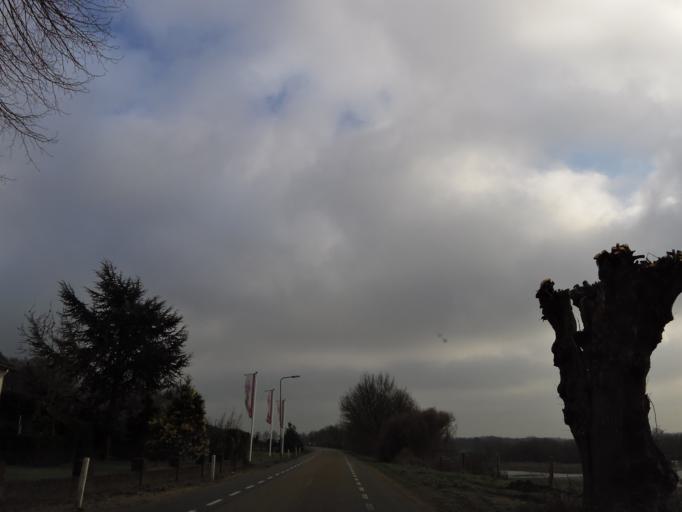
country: NL
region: Limburg
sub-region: Gemeente Gennep
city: Gennep
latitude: 51.7160
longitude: 5.9555
